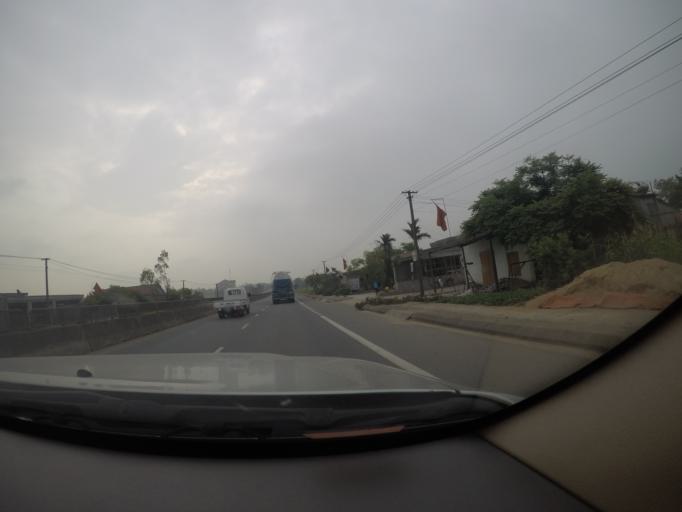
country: VN
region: Ha Tinh
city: Ky Anh
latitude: 18.1948
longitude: 106.1749
